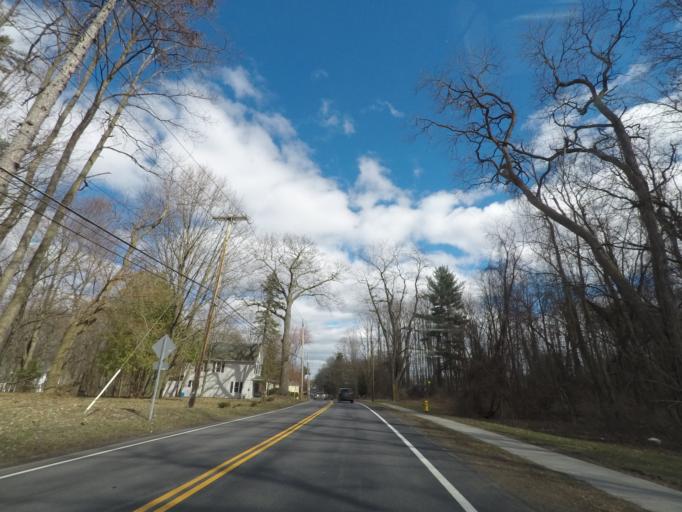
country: US
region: New York
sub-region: Albany County
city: Delmar
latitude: 42.6016
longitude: -73.7994
